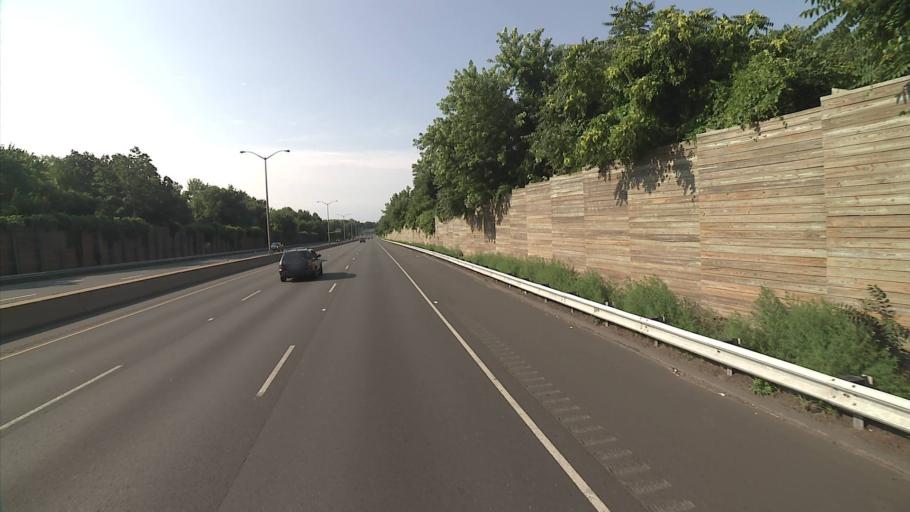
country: US
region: Connecticut
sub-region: Hartford County
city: Thompsonville
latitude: 42.0134
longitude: -72.5866
